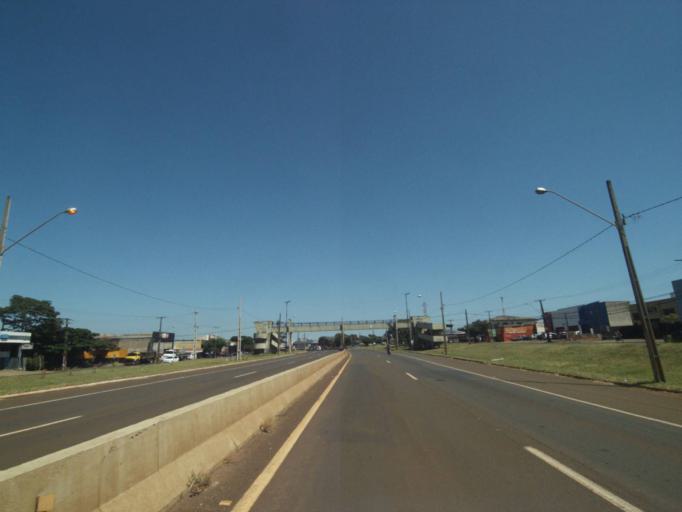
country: BR
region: Parana
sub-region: Londrina
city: Londrina
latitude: -23.3644
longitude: -51.1449
